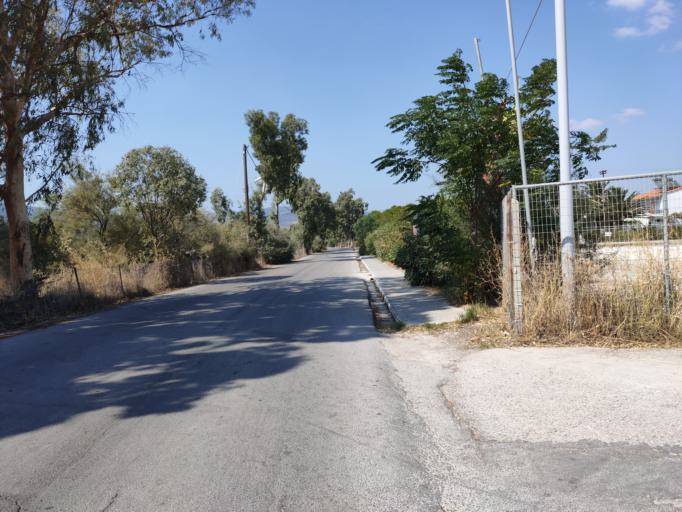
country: GR
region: North Aegean
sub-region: Nomos Lesvou
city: Kalloni
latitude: 39.2071
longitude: 26.2091
